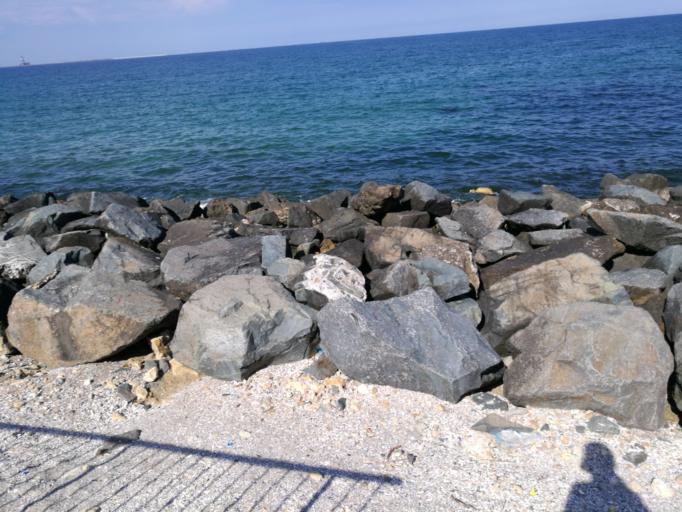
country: RO
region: Constanta
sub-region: Oras Eforie
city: Eforie
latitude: 44.0410
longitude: 28.6486
